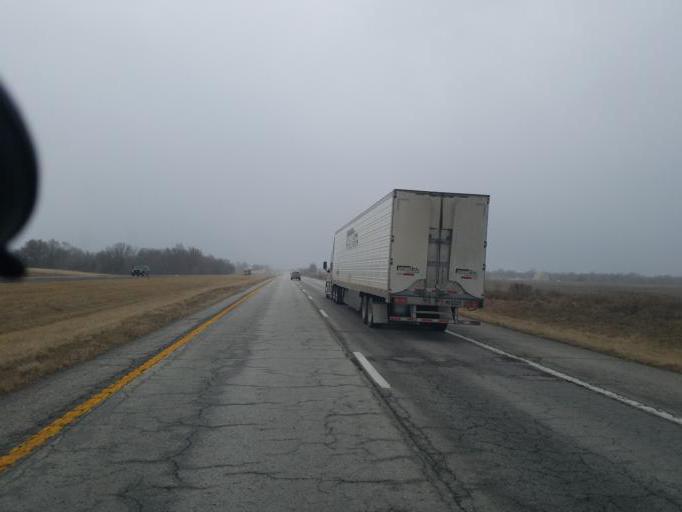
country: US
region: Missouri
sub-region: Macon County
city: La Plata
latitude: 39.9141
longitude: -92.4741
